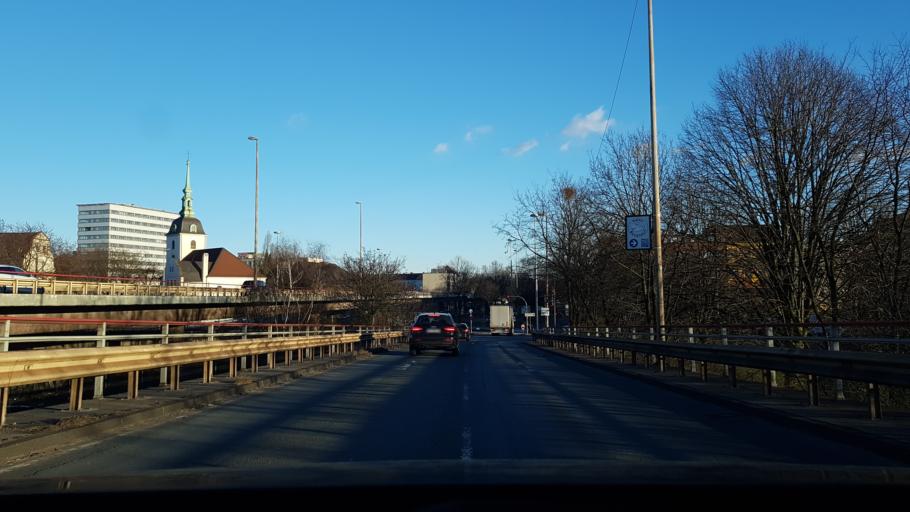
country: DE
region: North Rhine-Westphalia
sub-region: Regierungsbezirk Dusseldorf
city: Duisburg
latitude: 51.4324
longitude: 6.7542
